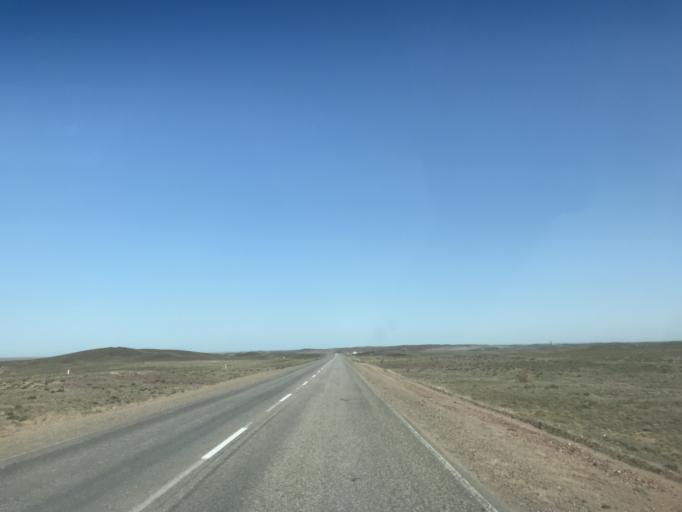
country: KZ
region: Zhambyl
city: Mynaral
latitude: 45.4651
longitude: 73.5699
